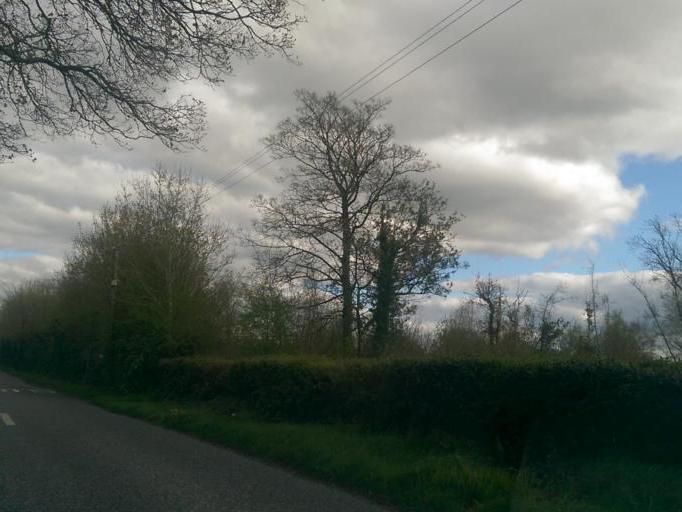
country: IE
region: Connaught
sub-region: County Galway
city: Ballinasloe
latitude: 53.4183
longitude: -8.3823
